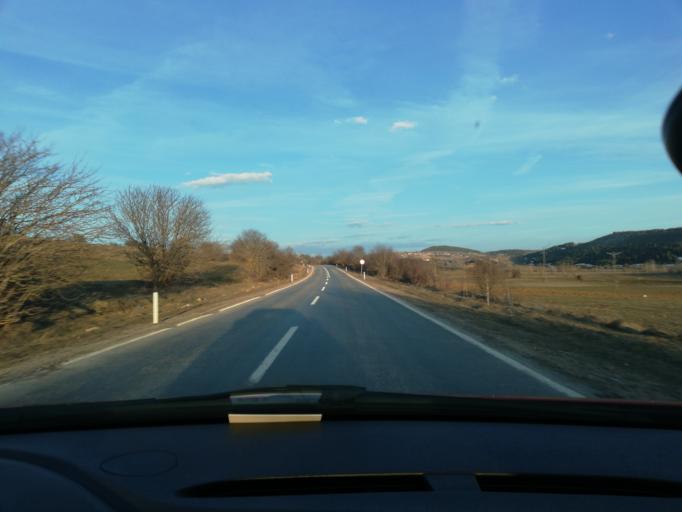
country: TR
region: Kastamonu
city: Agli
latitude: 41.6921
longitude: 33.5978
